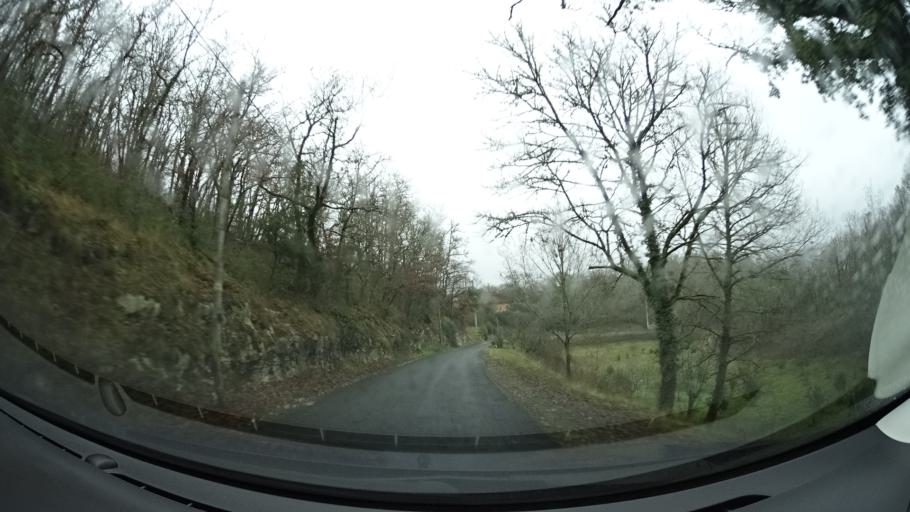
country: FR
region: Aquitaine
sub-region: Departement de la Dordogne
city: Cenac-et-Saint-Julien
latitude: 44.7653
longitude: 1.1696
